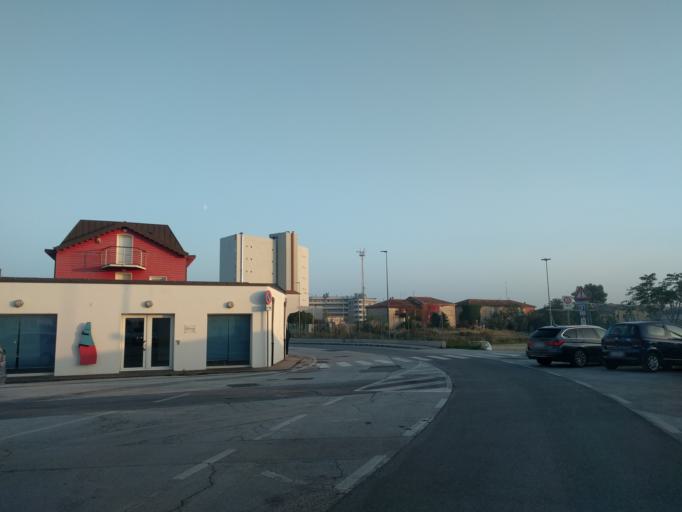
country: IT
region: The Marches
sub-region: Provincia di Ancona
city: Senigallia
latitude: 43.7206
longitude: 13.2185
